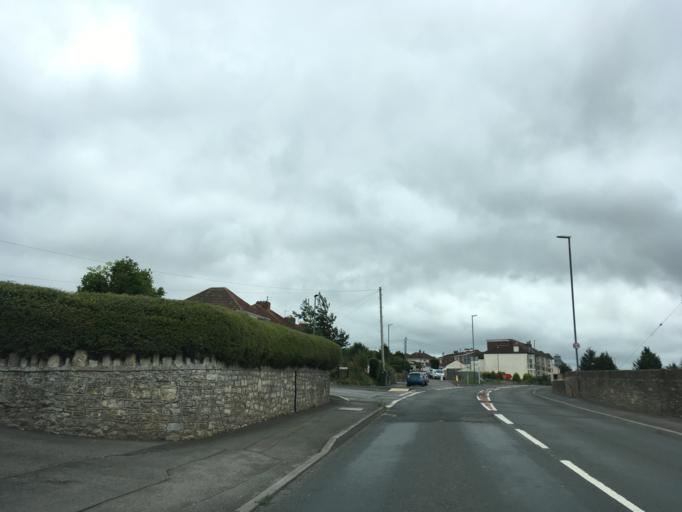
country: GB
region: England
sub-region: Bath and North East Somerset
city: Keynsham
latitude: 51.4064
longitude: -2.4927
